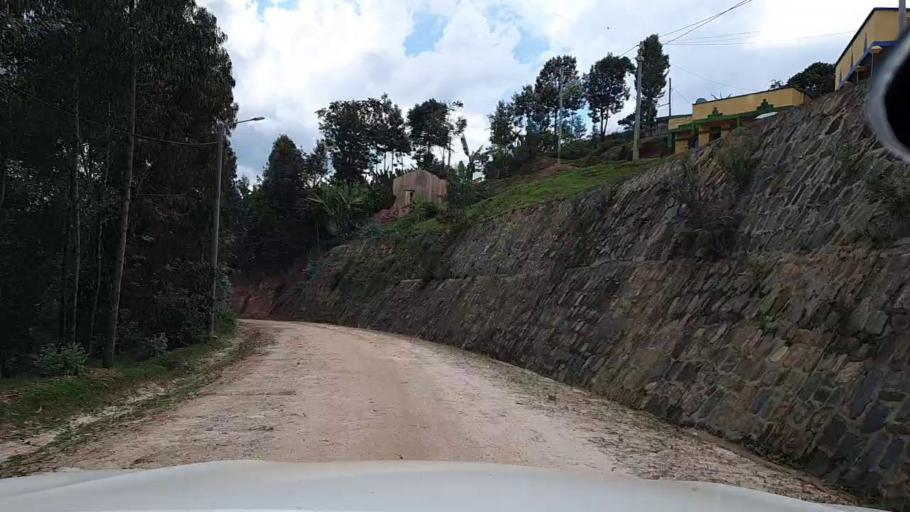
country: RW
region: Southern Province
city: Nzega
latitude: -2.6899
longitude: 29.4440
